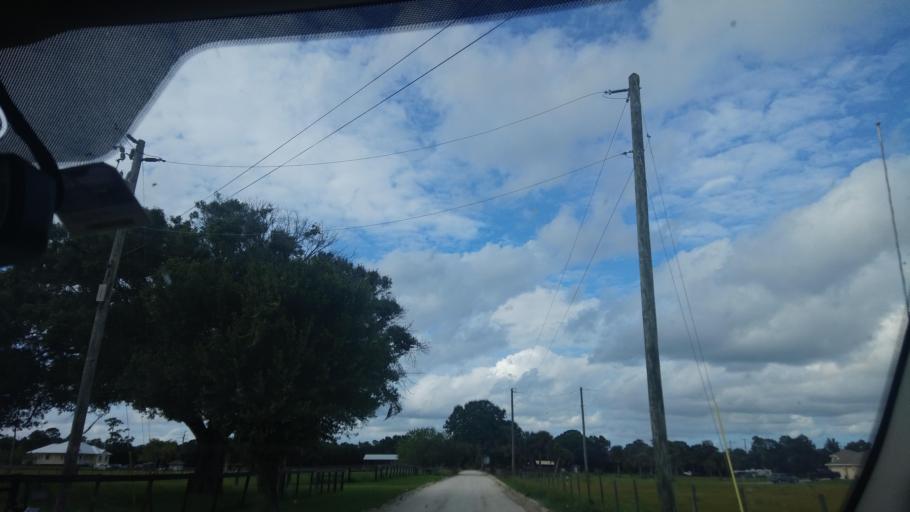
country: US
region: Florida
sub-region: Indian River County
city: Fellsmere
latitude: 27.7838
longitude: -80.5929
